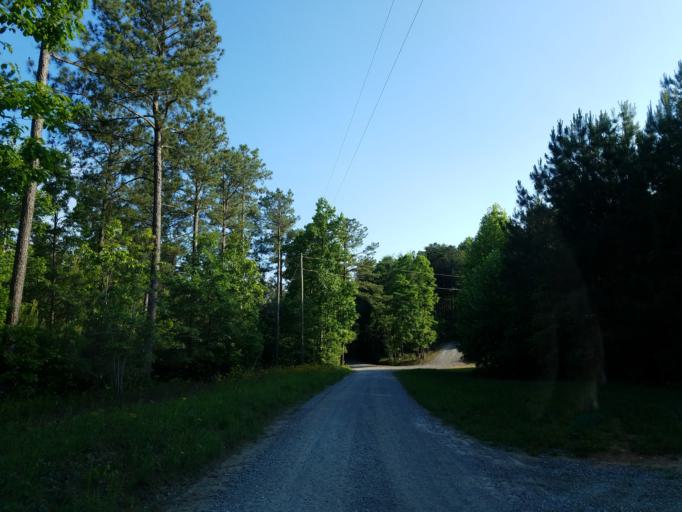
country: US
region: Georgia
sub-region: Pickens County
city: Nelson
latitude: 34.3609
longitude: -84.3263
